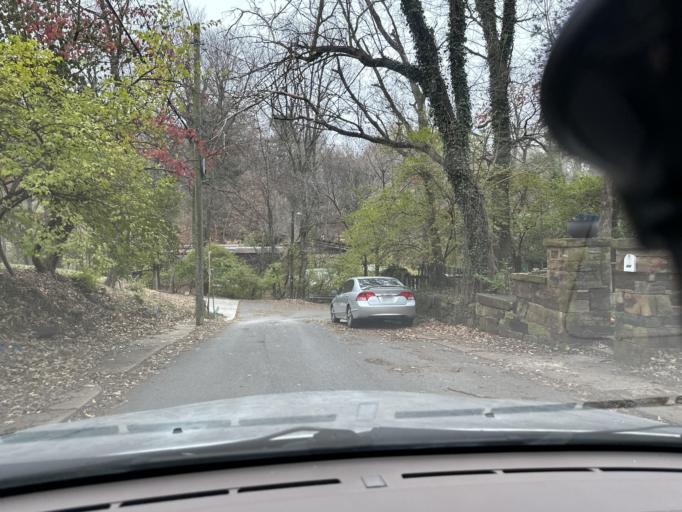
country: US
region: Arkansas
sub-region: Washington County
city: Fayetteville
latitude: 36.0652
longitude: -94.1551
